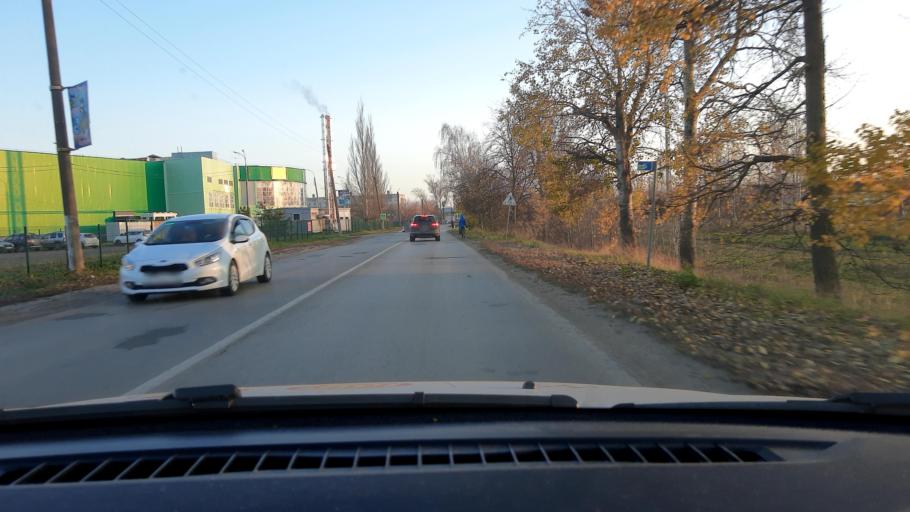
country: RU
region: Nizjnij Novgorod
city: Volodarsk
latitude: 56.2406
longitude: 43.1835
